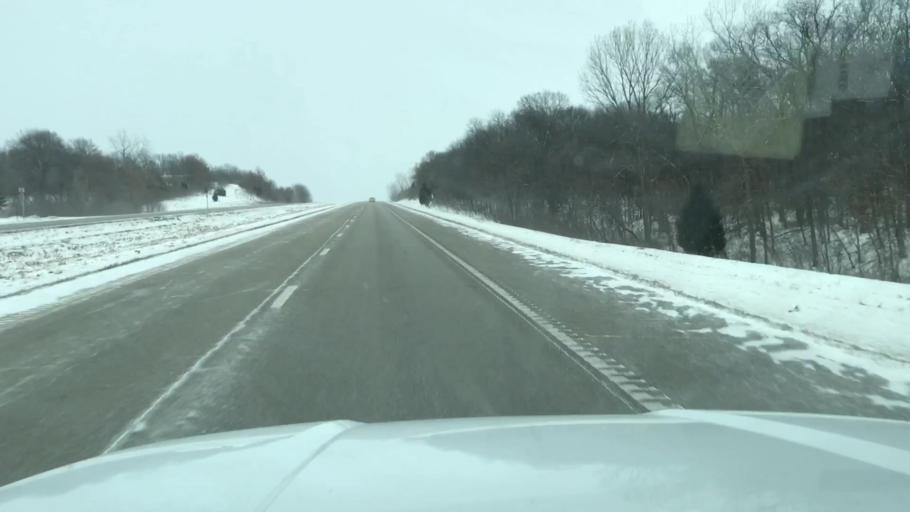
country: US
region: Missouri
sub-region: Clinton County
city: Gower
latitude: 39.7522
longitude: -94.5919
